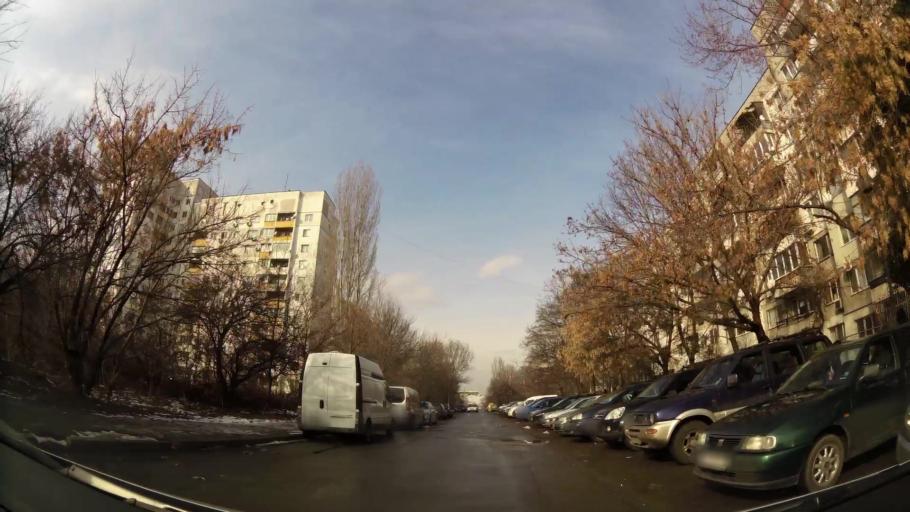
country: BG
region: Sofia-Capital
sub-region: Stolichna Obshtina
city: Sofia
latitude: 42.7152
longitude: 23.2660
